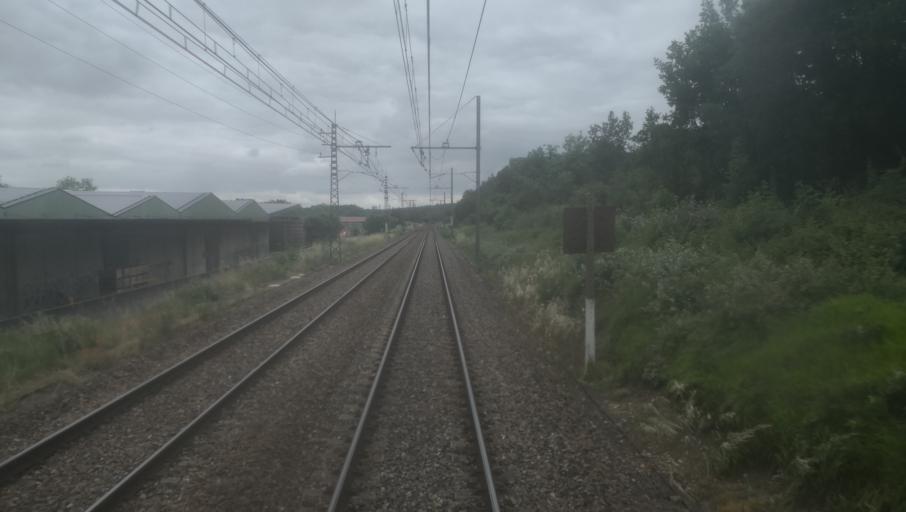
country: FR
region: Midi-Pyrenees
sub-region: Departement du Tarn-et-Garonne
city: Verdun-sur-Garonne
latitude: 43.8865
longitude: 1.2708
